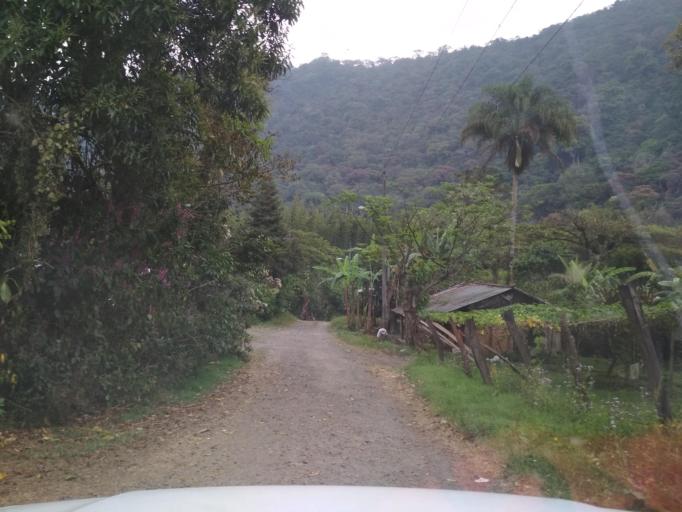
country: MX
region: Veracruz
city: Cuautlapan
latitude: 18.8670
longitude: -97.0128
